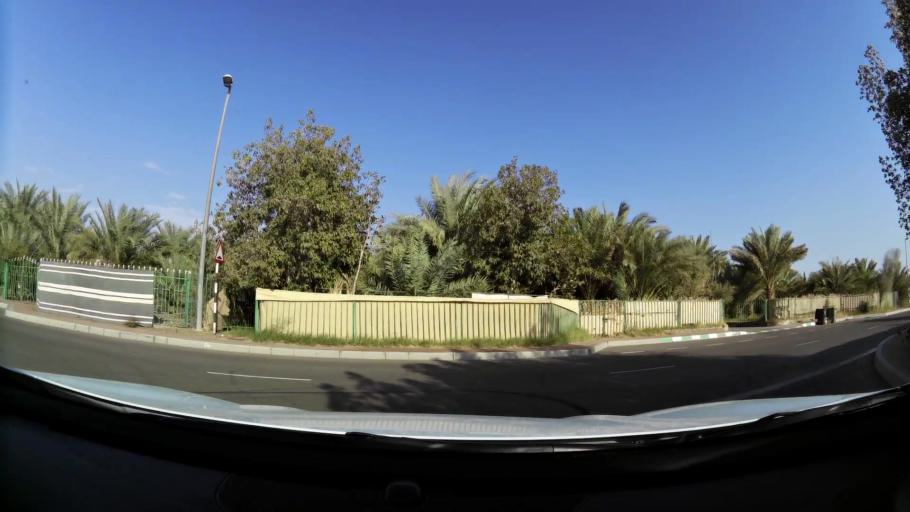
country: AE
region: Abu Dhabi
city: Al Ain
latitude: 24.0593
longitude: 55.8479
